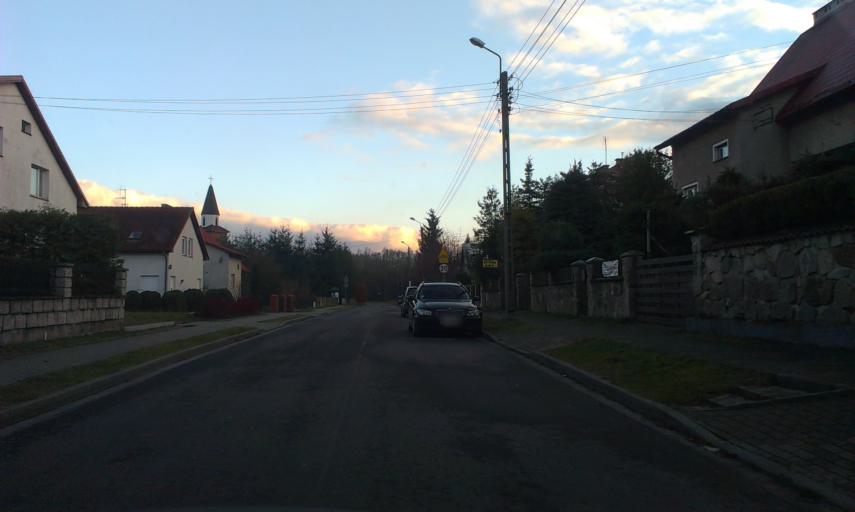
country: PL
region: West Pomeranian Voivodeship
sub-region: Powiat szczecinecki
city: Szczecinek
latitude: 53.6821
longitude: 16.7177
